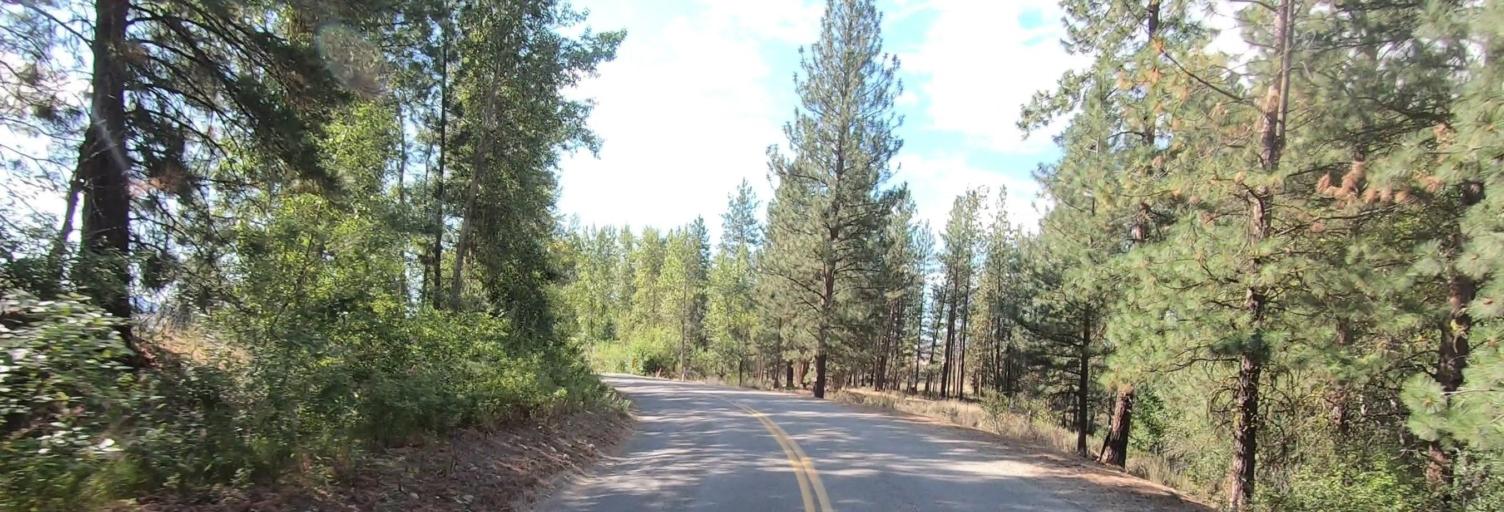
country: US
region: Washington
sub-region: Okanogan County
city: Brewster
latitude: 48.5291
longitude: -120.1782
